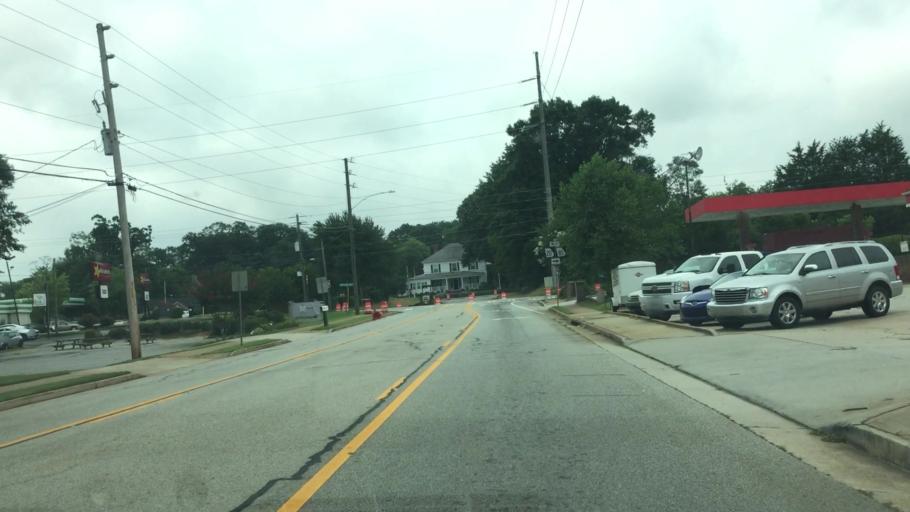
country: US
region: Georgia
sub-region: Henry County
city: McDonough
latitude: 33.4485
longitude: -84.1416
